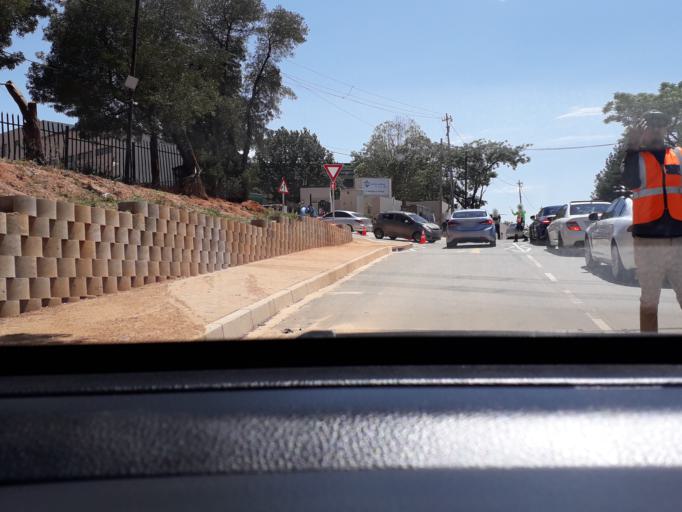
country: ZA
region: Gauteng
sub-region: City of Johannesburg Metropolitan Municipality
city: Modderfontein
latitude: -26.0901
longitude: 28.0633
